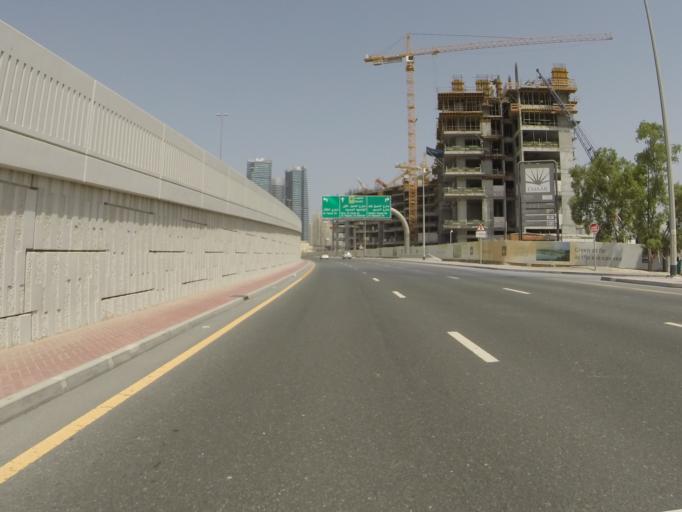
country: AE
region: Dubai
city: Dubai
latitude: 25.0767
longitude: 55.1607
